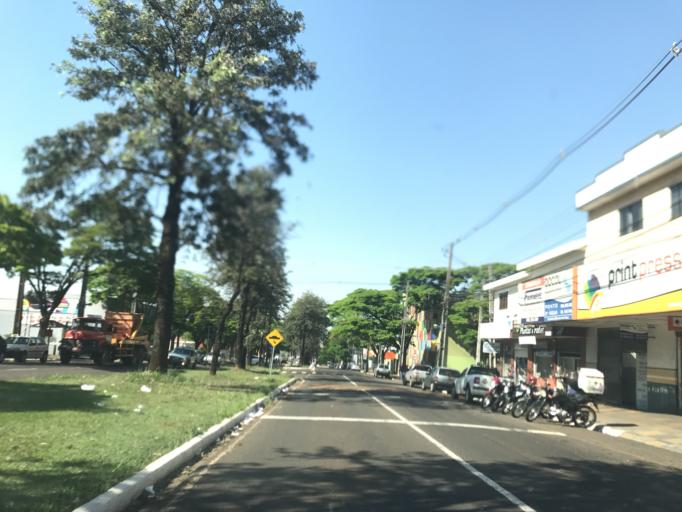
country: BR
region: Parana
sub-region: Maringa
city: Maringa
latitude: -23.4449
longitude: -51.9327
